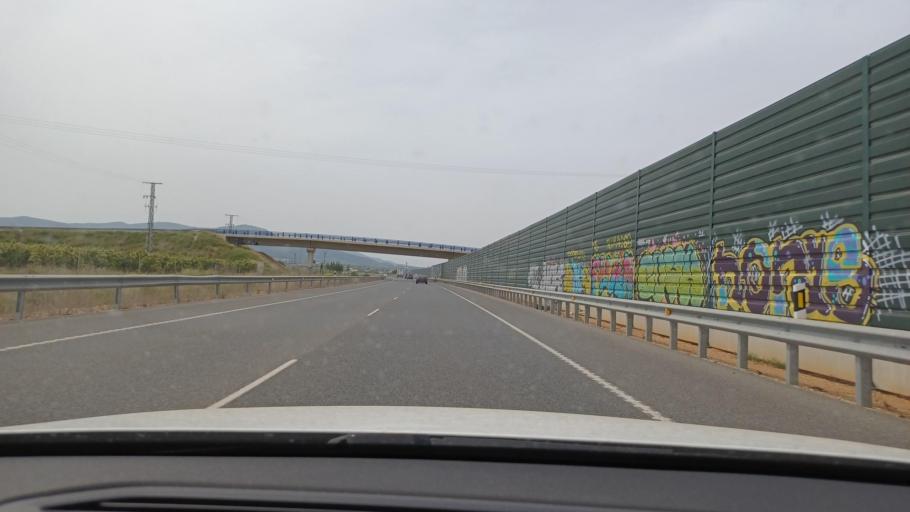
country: ES
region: Valencia
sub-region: Provincia de Castello
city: Benicarlo
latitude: 40.4244
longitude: 0.3934
